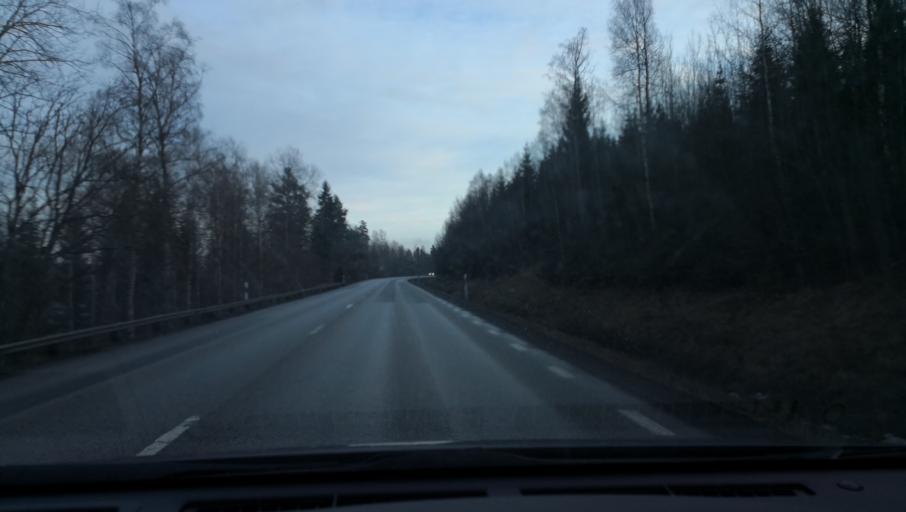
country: SE
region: OErebro
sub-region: Degerfors Kommun
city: Degerfors
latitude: 59.1194
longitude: 14.5322
